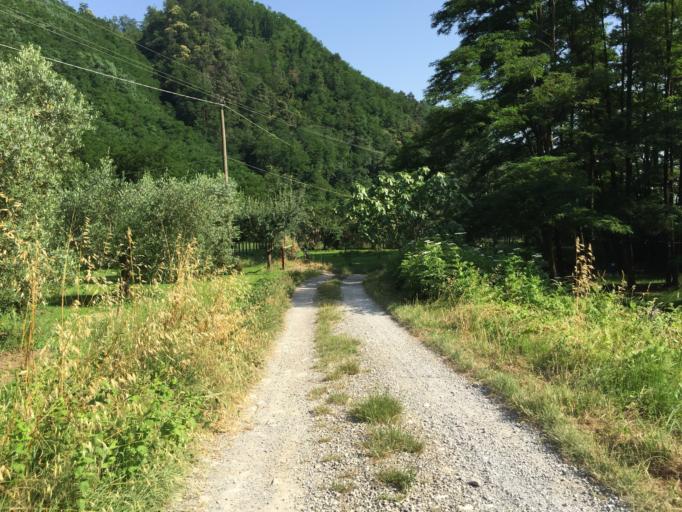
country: IT
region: Tuscany
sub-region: Provincia di Pistoia
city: Uzzano
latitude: 43.9206
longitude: 10.6950
